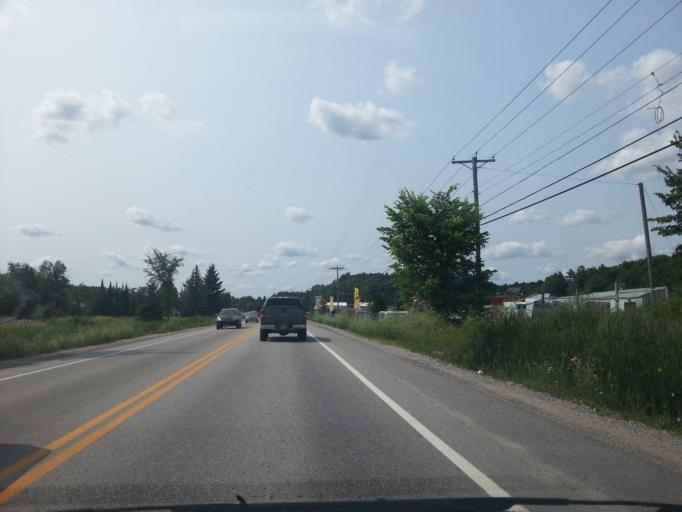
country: CA
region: Quebec
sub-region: Outaouais
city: Wakefield
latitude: 45.6164
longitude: -75.9184
